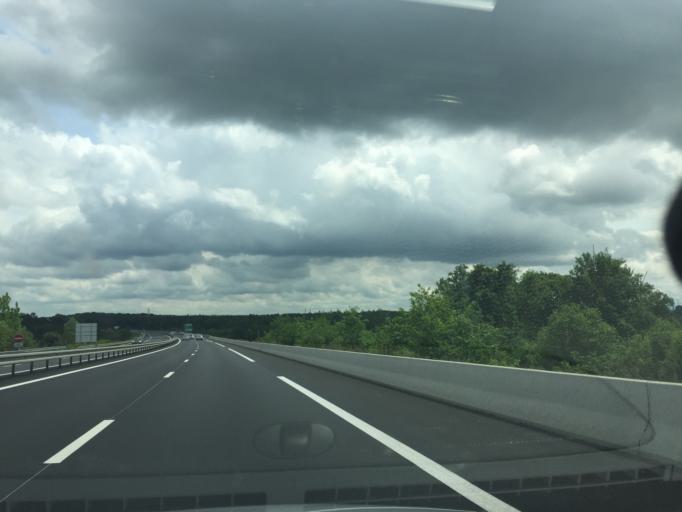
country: FR
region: Pays de la Loire
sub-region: Departement de la Sarthe
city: Change
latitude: 48.0127
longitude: 0.2971
